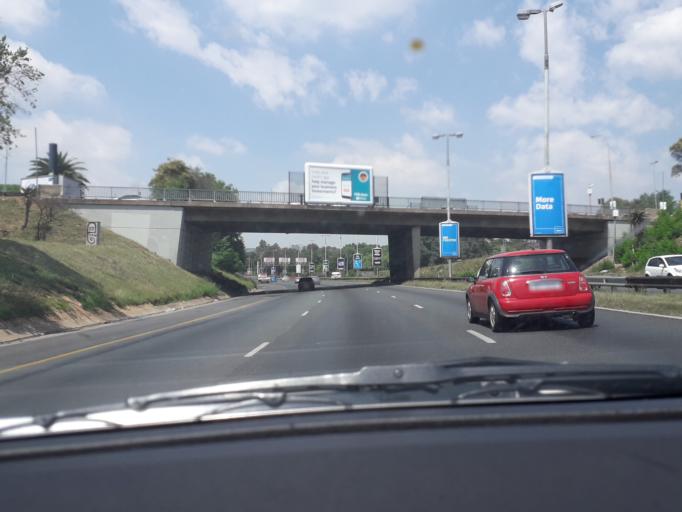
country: ZA
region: Gauteng
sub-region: City of Johannesburg Metropolitan Municipality
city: Johannesburg
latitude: -26.1458
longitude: 28.0587
